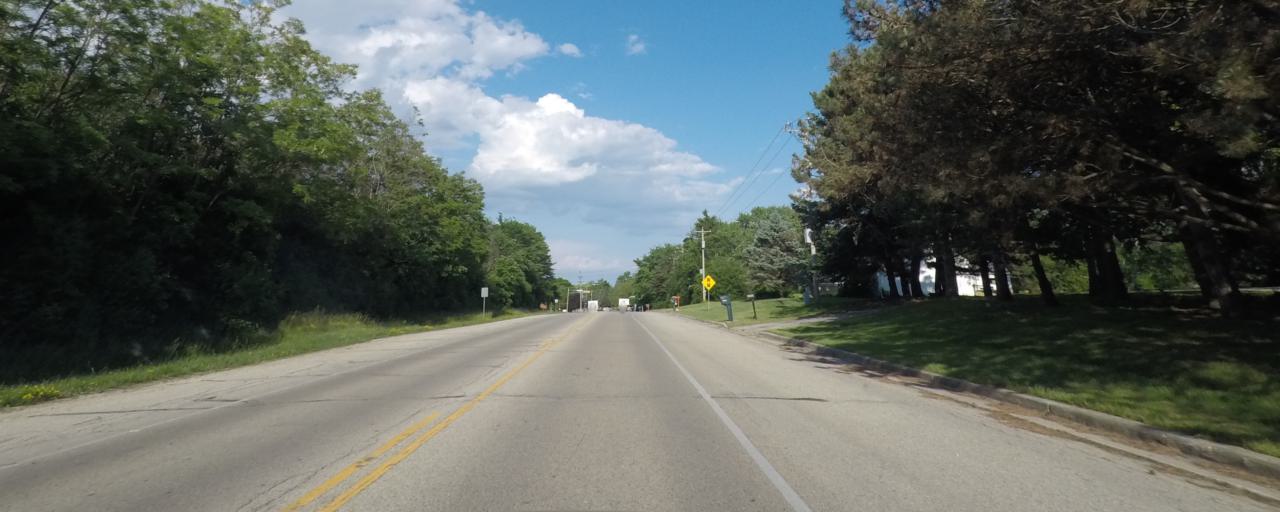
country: US
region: Wisconsin
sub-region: Waukesha County
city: New Berlin
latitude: 42.9552
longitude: -88.0921
